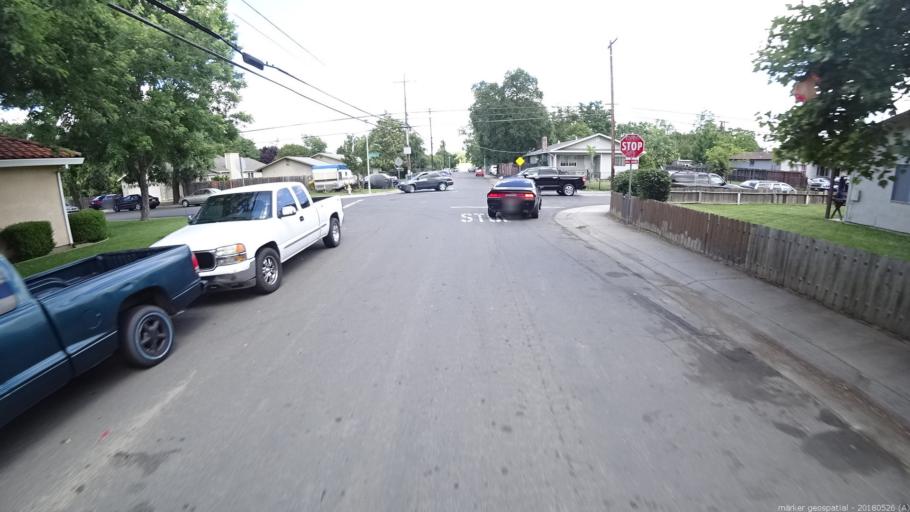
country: US
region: California
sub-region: Sacramento County
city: Sacramento
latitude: 38.6121
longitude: -121.4720
